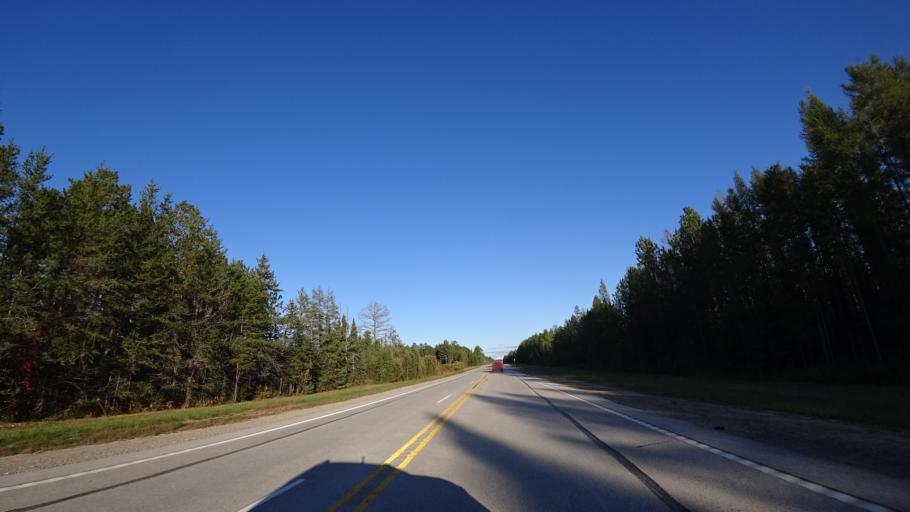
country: US
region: Michigan
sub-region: Schoolcraft County
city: Manistique
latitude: 46.3454
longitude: -86.0888
